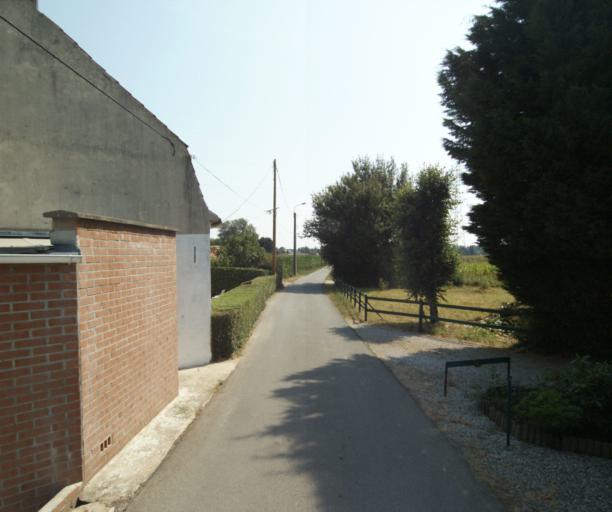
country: FR
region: Nord-Pas-de-Calais
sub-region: Departement du Nord
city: Wambrechies
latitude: 50.6834
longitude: 3.0311
